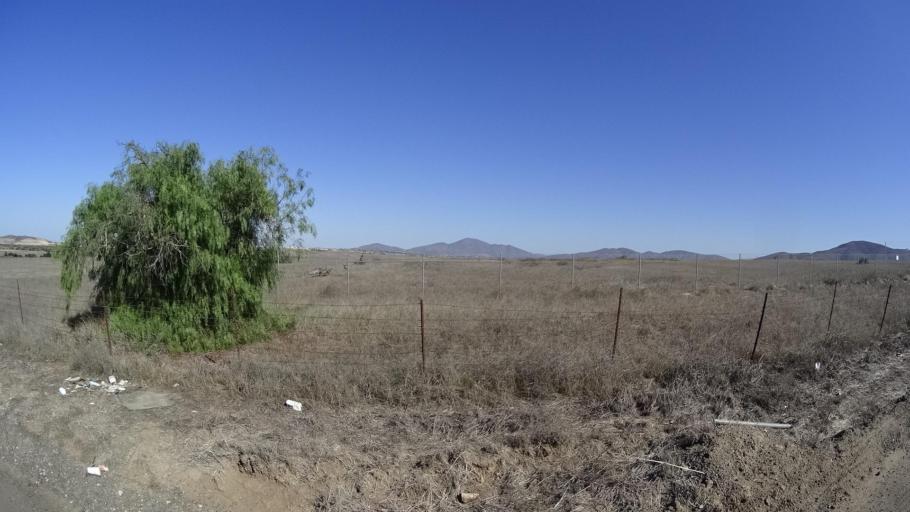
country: MX
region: Baja California
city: Tijuana
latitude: 32.5786
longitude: -116.9484
